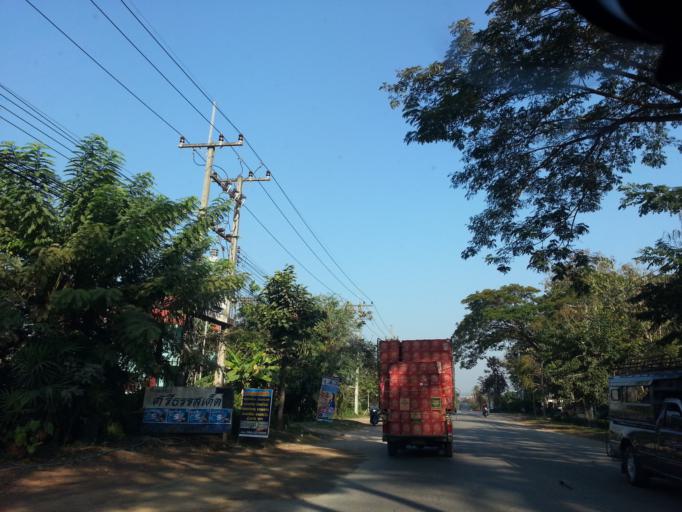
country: TH
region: Chiang Mai
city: San Sai
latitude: 18.8811
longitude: 99.0348
